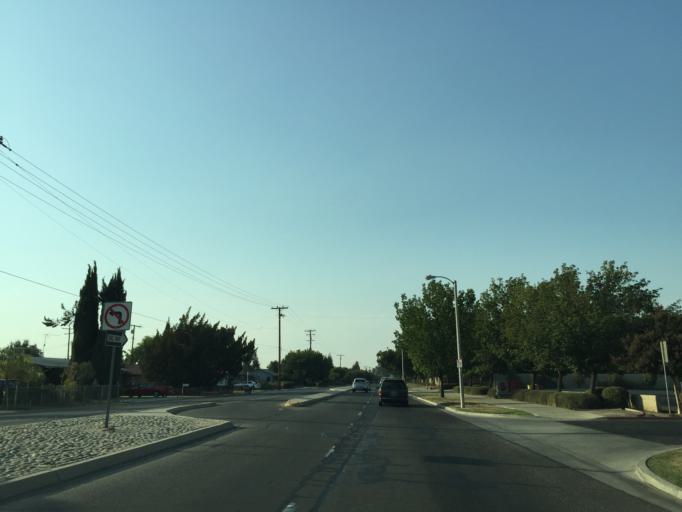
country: US
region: California
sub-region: Tulare County
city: Visalia
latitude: 36.3432
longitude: -119.2788
